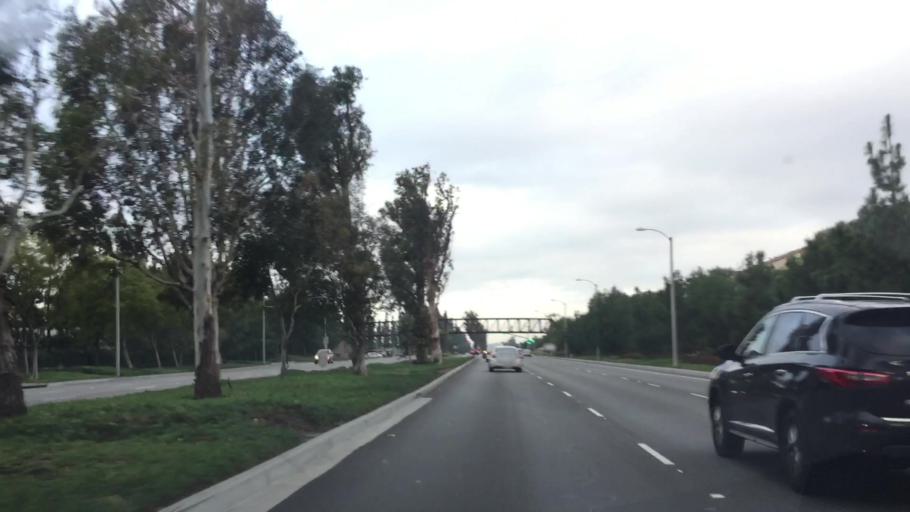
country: US
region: California
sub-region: Orange County
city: North Tustin
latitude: 33.7058
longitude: -117.7485
